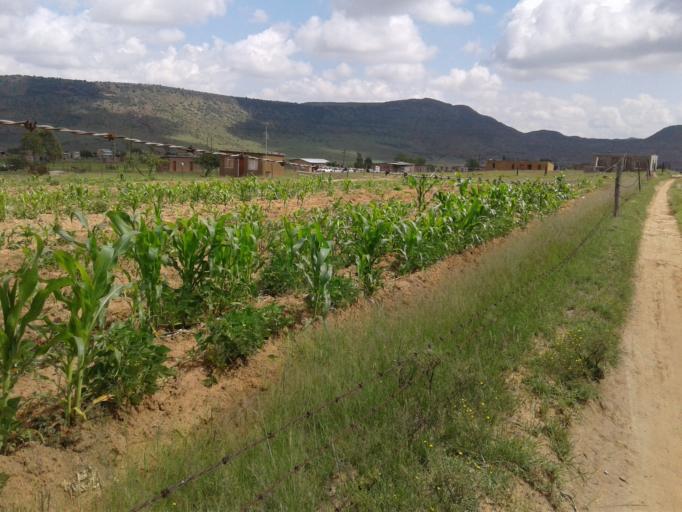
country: LS
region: Mafeteng
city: Mafeteng
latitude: -29.7529
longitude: 27.1120
